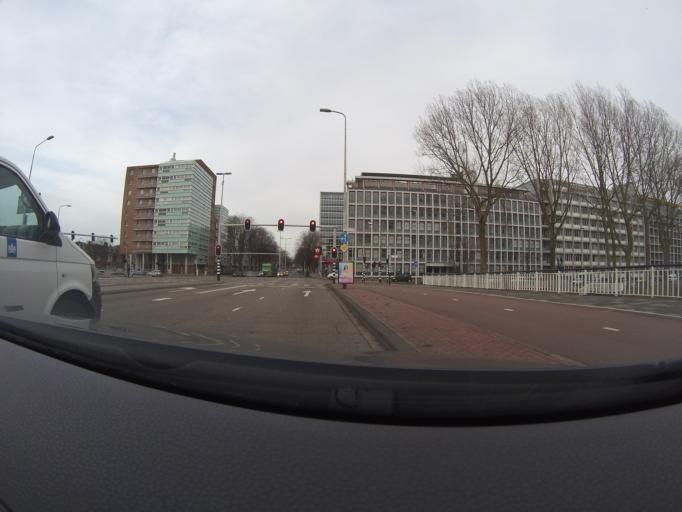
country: NL
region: South Holland
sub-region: Gemeente Den Haag
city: Scheveningen
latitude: 52.0850
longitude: 4.2733
